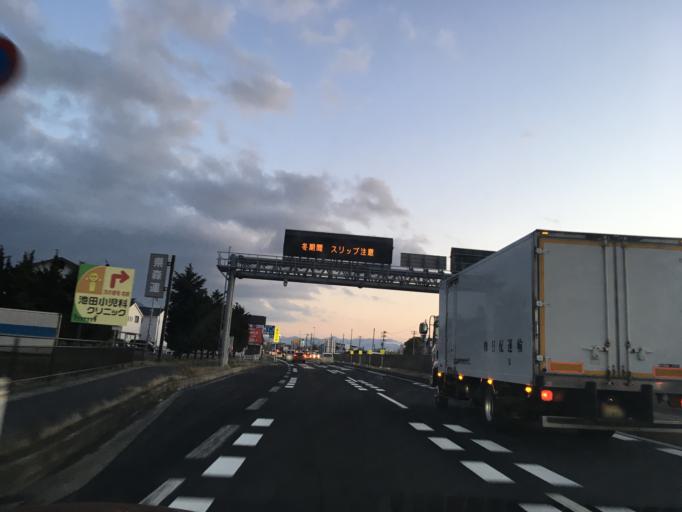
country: JP
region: Yamagata
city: Yamagata-shi
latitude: 38.2068
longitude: 140.3158
